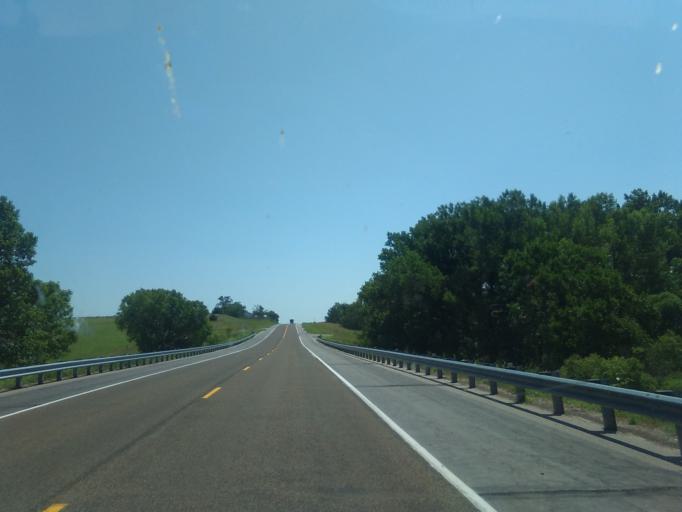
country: US
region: Nebraska
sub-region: Hitchcock County
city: Trenton
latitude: 40.1762
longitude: -101.1032
